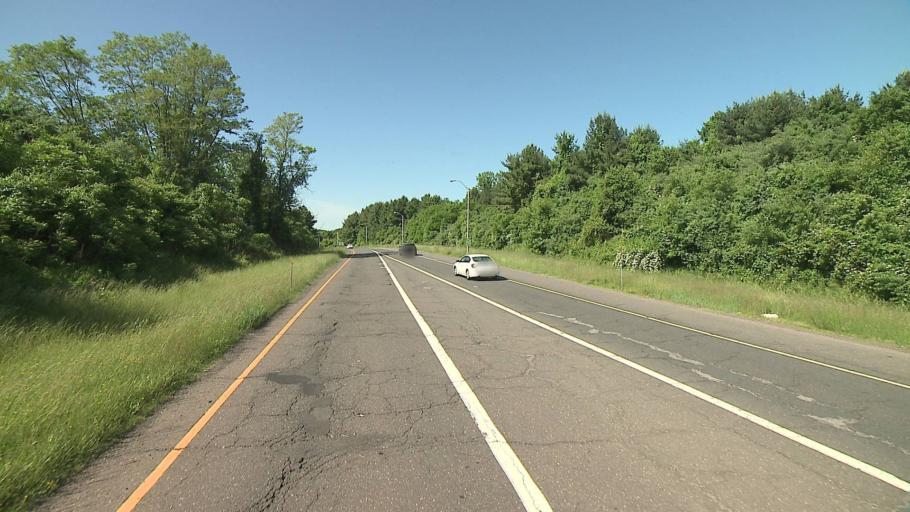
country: US
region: Connecticut
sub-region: Hartford County
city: East Hartford
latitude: 41.7797
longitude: -72.5722
